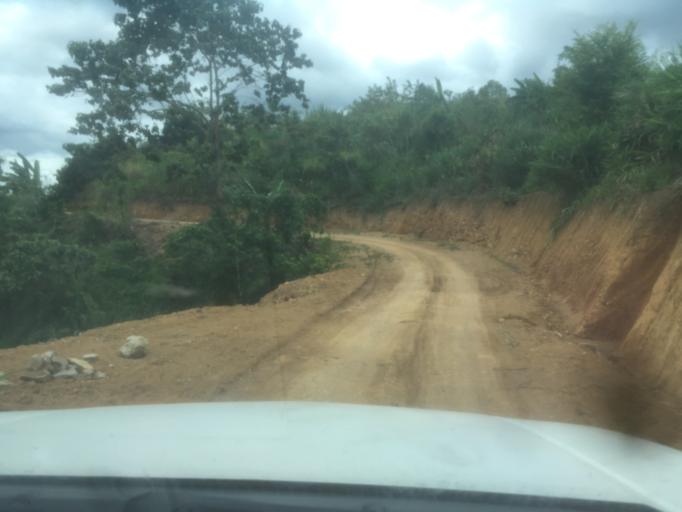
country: LA
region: Phongsali
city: Khoa
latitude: 20.9259
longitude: 102.5429
